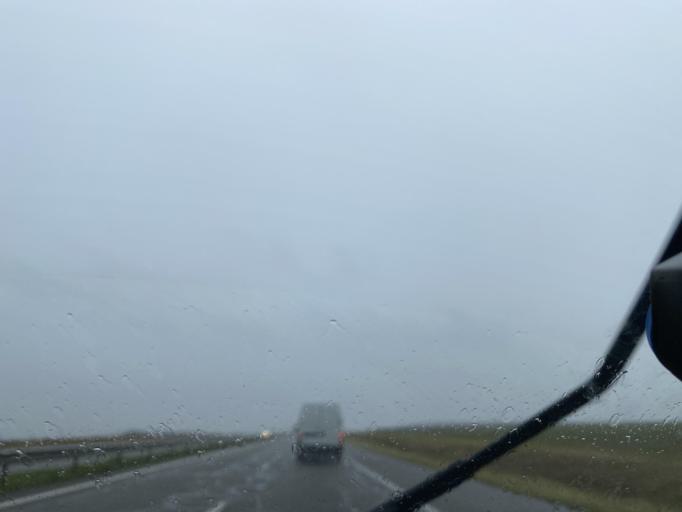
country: FR
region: Centre
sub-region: Departement d'Eure-et-Loir
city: Villemeux-sur-Eure
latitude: 48.6379
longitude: 1.4085
